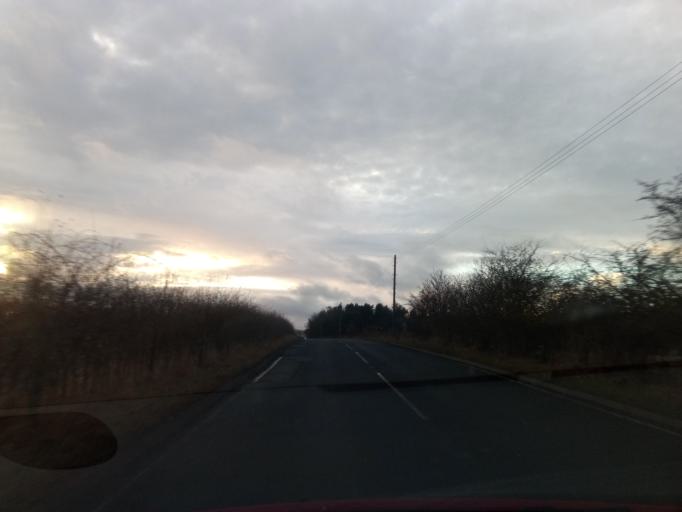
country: GB
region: England
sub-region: Newcastle upon Tyne
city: Dinnington
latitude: 55.0747
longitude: -1.6813
